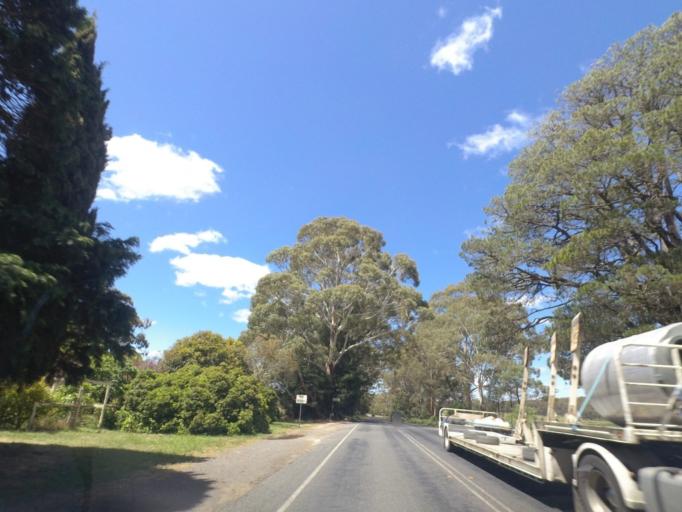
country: AU
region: Victoria
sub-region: Mount Alexander
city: Castlemaine
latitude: -37.3159
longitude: 144.2208
